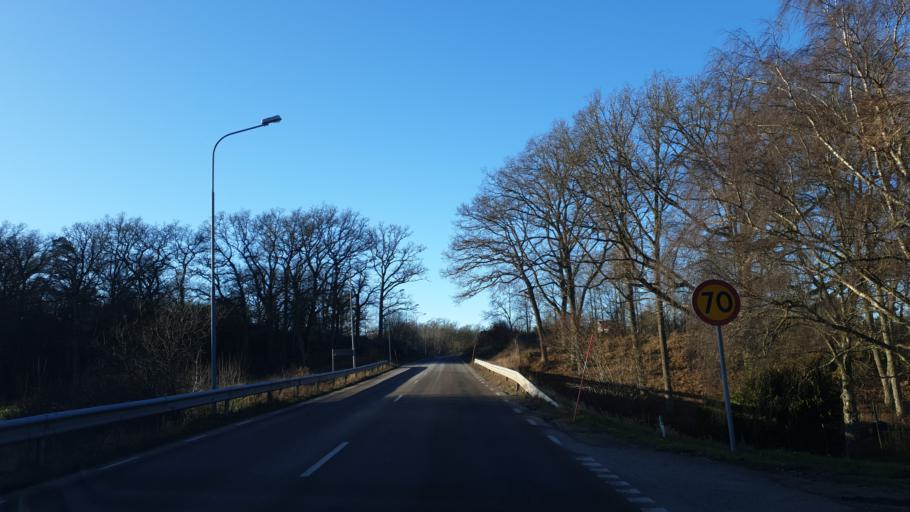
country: SE
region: Blekinge
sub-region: Ronneby Kommun
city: Ronneby
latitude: 56.1973
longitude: 15.3202
